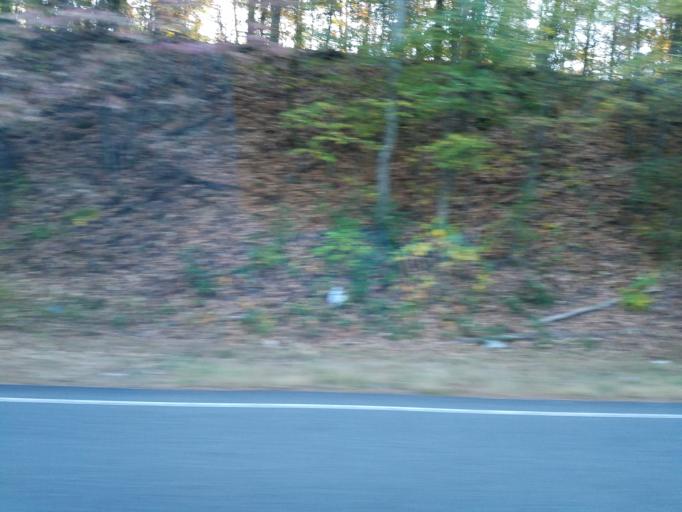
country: US
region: Georgia
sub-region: Bartow County
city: Adairsville
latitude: 34.3592
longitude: -84.9393
